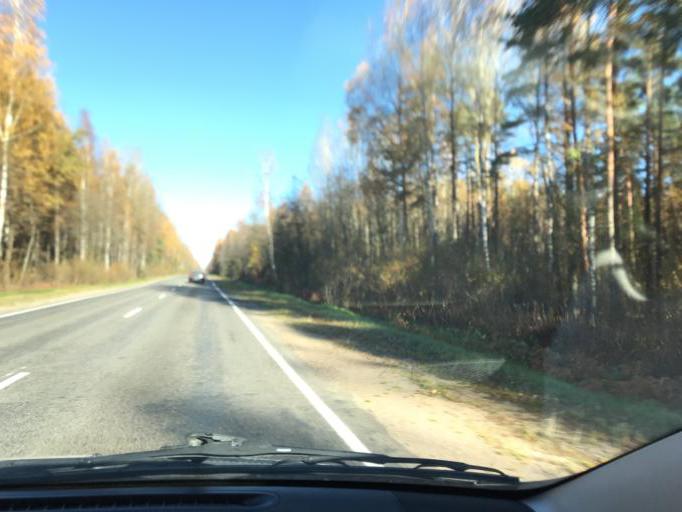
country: BY
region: Vitebsk
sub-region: Ushatski Rayon
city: Ushachy
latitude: 55.0609
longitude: 28.7527
